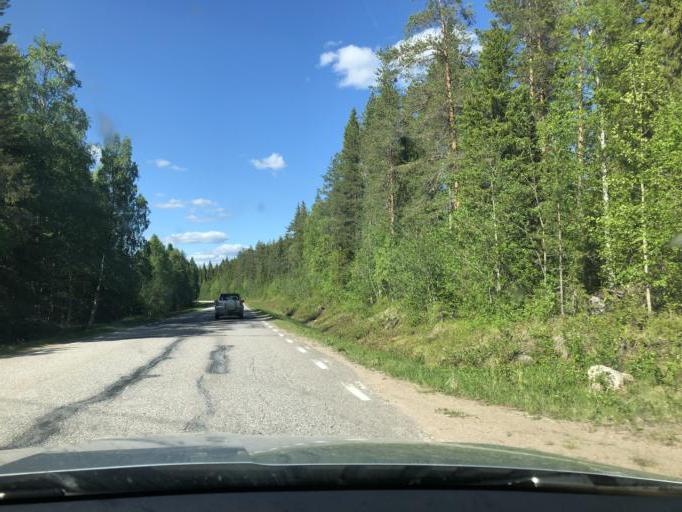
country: SE
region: Norrbotten
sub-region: Kalix Kommun
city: Kalix
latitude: 65.9451
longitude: 23.1517
